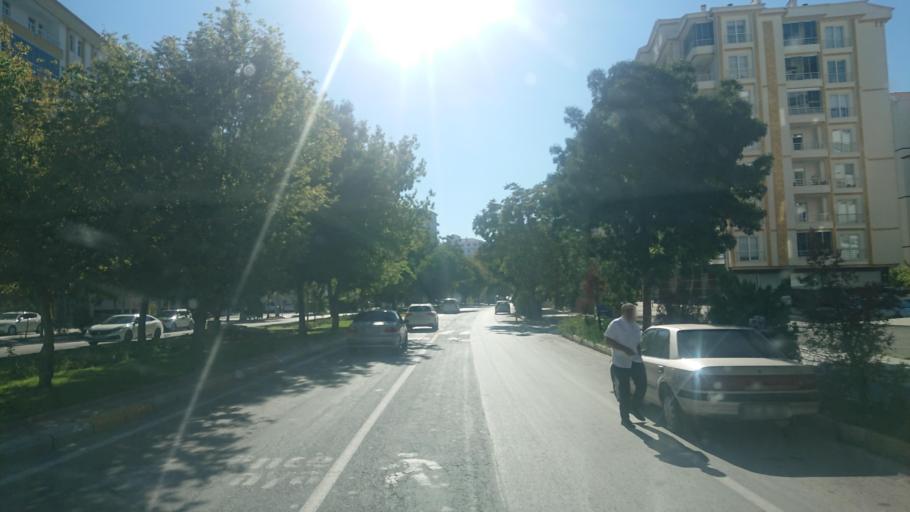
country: TR
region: Aksaray
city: Aksaray
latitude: 38.3642
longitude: 34.0186
